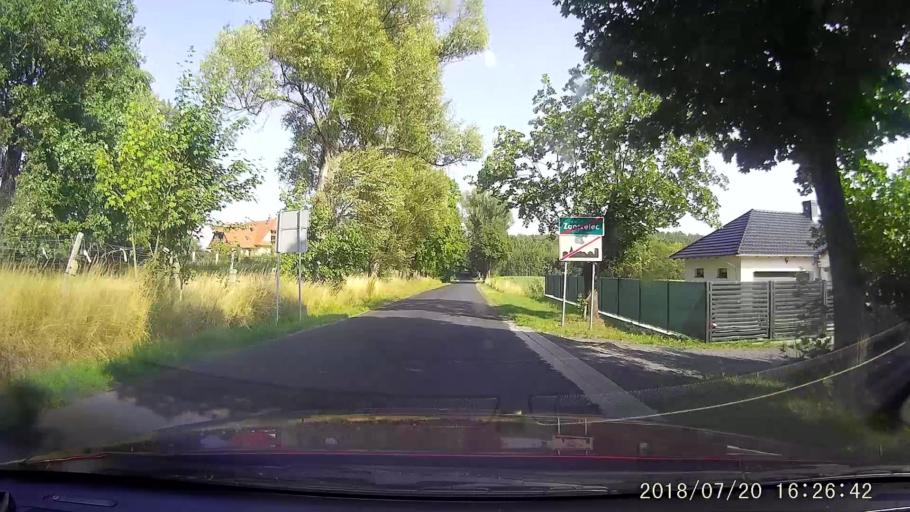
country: PL
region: Lower Silesian Voivodeship
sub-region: Powiat zgorzelecki
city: Lagow
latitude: 51.1291
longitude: 15.0384
